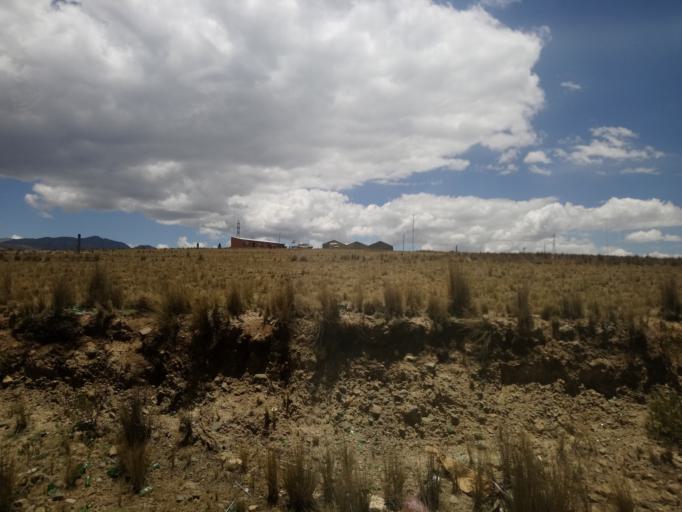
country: BO
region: La Paz
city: La Paz
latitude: -16.4409
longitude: -68.1635
